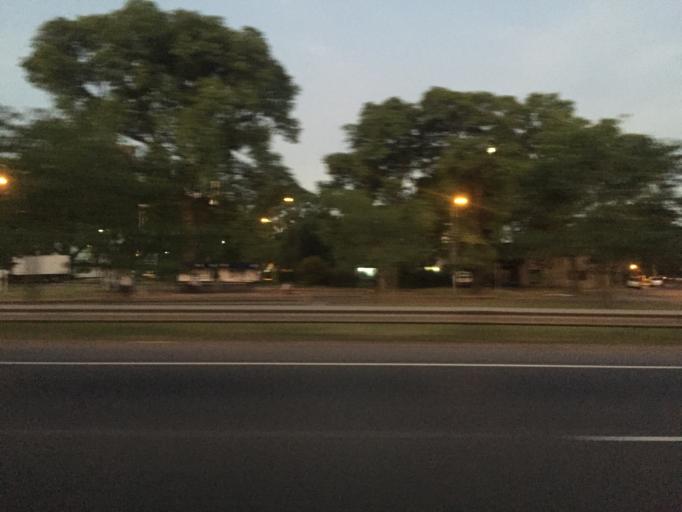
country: AR
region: Buenos Aires F.D.
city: Villa Lugano
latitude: -34.6806
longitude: -58.4935
